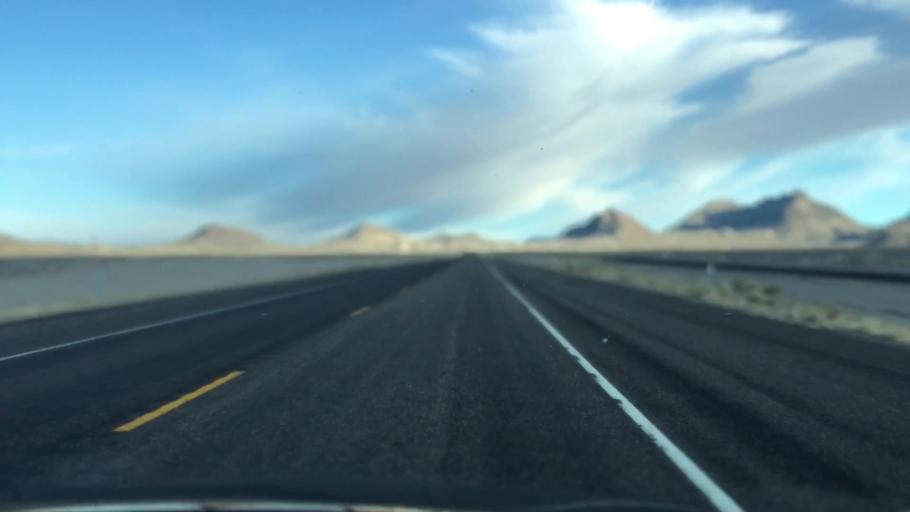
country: US
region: Nevada
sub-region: Nye County
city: Tonopah
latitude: 38.0863
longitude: -117.2853
